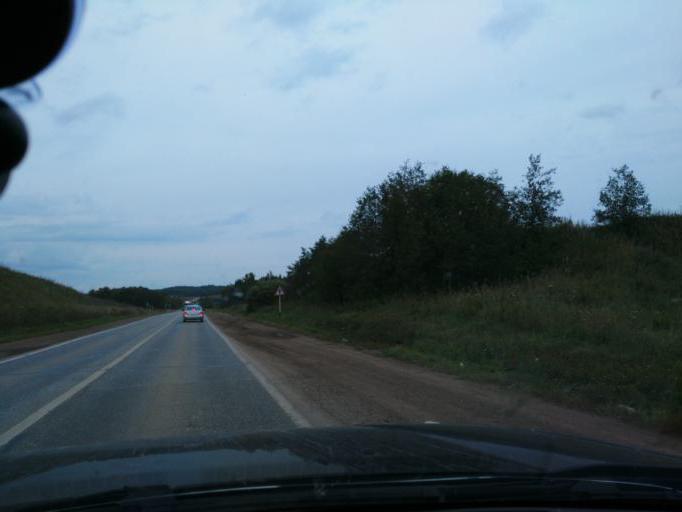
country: RU
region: Perm
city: Chernushka
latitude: 56.5555
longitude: 56.1110
